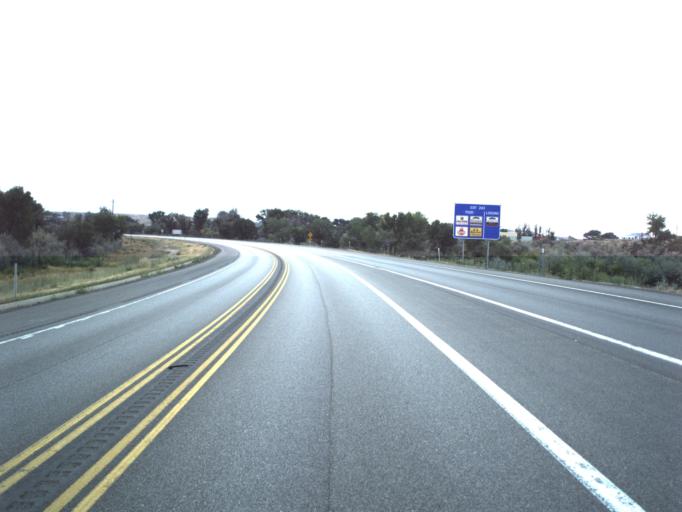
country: US
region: Utah
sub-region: Carbon County
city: Price
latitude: 39.5858
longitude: -110.8065
